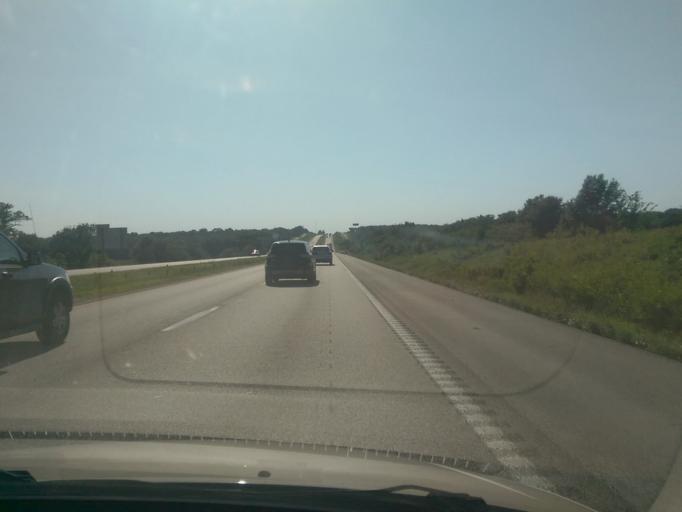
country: US
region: Missouri
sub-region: Saline County
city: Sweet Springs
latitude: 38.9745
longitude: -93.3566
